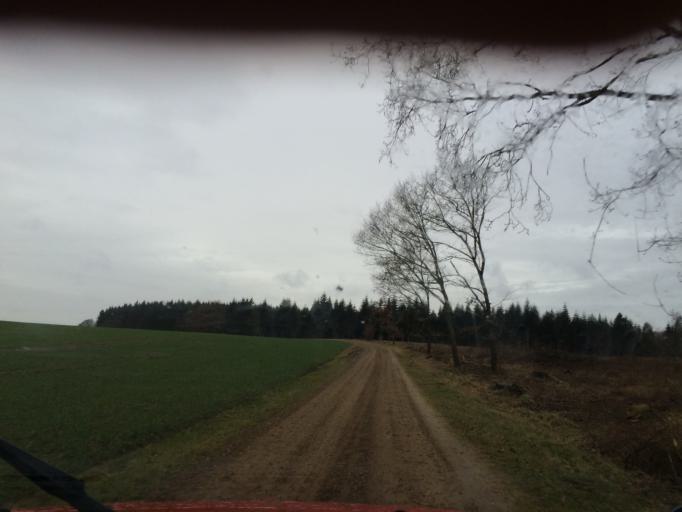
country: DK
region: Central Jutland
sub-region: Silkeborg Kommune
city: Virklund
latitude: 56.0252
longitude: 9.4796
